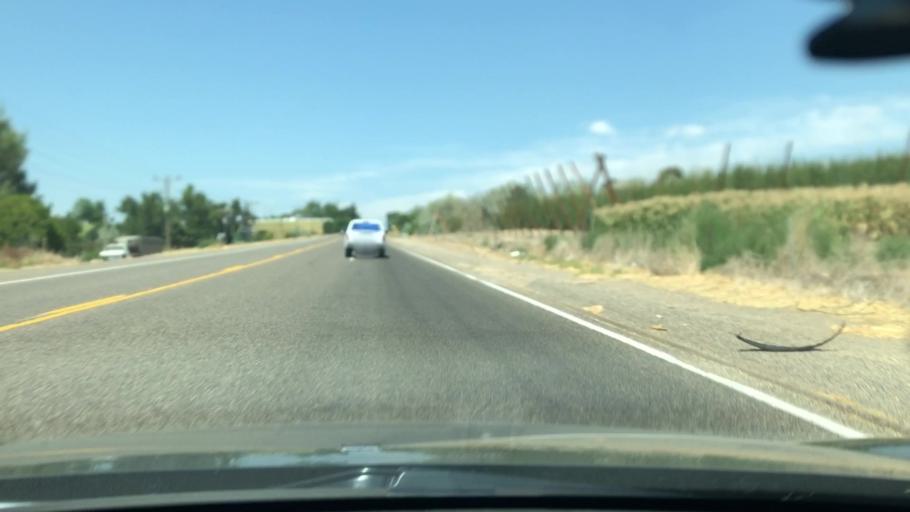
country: US
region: Idaho
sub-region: Canyon County
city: Wilder
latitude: 43.6556
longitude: -116.9118
